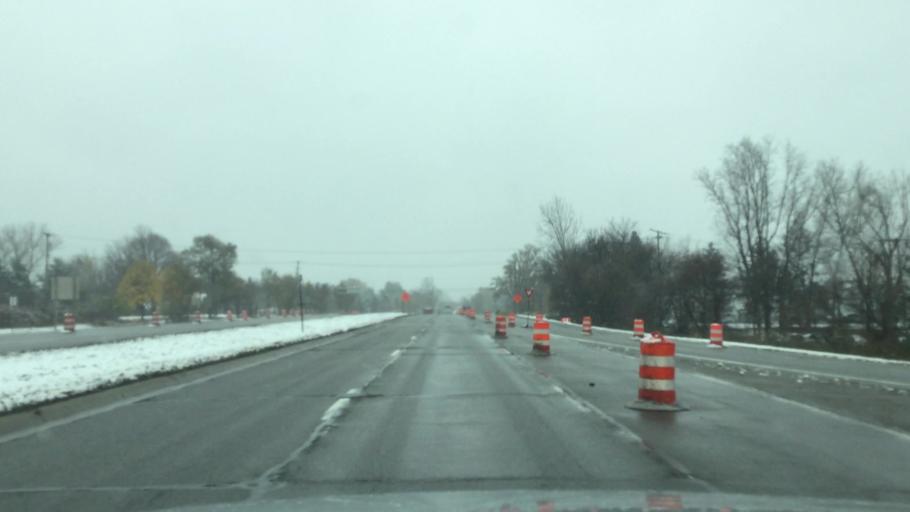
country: US
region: Michigan
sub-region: Oakland County
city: Auburn Hills
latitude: 42.6915
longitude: -83.2416
